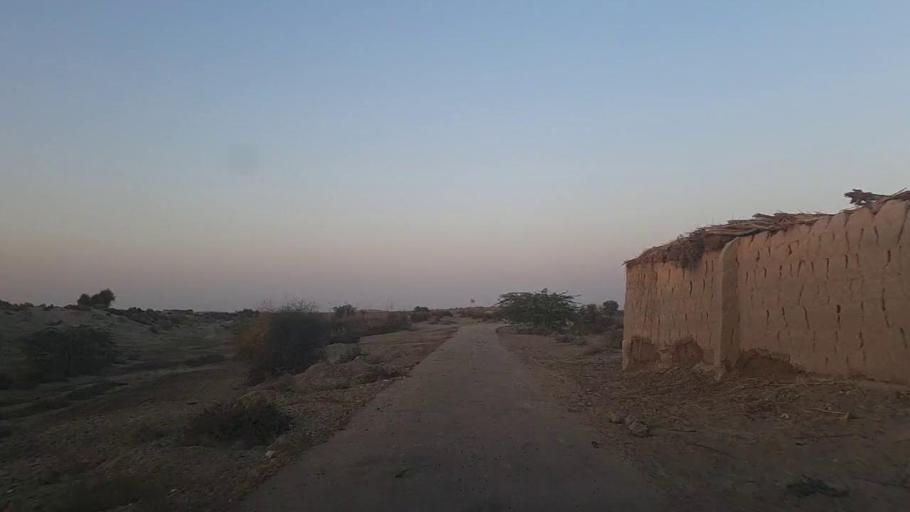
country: PK
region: Sindh
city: Jam Sahib
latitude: 26.3868
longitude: 68.6955
